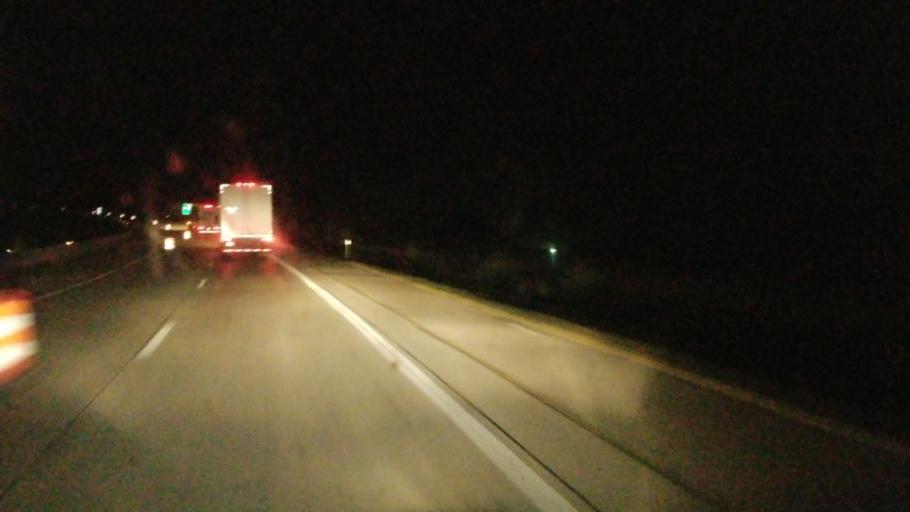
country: US
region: Indiana
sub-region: Allen County
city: New Haven
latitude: 41.1240
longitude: -84.9955
